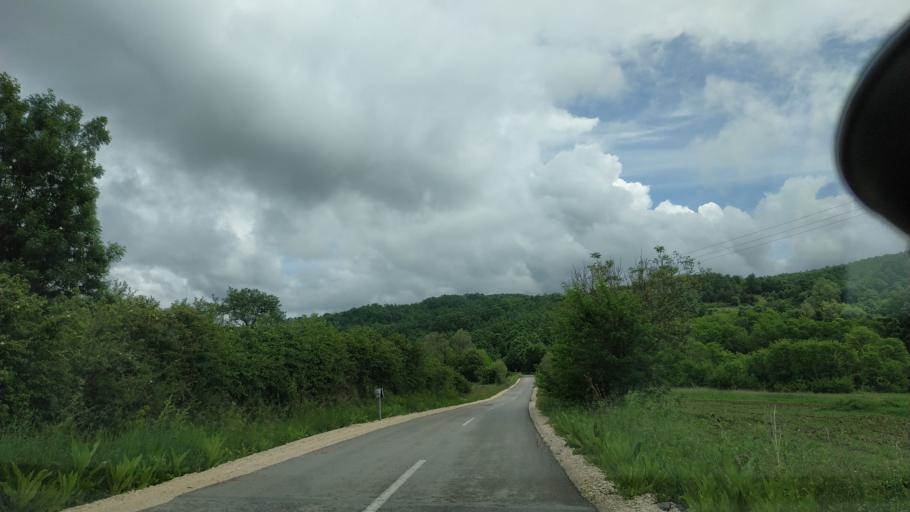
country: RS
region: Central Serbia
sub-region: Zajecarski Okrug
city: Soko Banja
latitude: 43.6579
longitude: 21.9058
